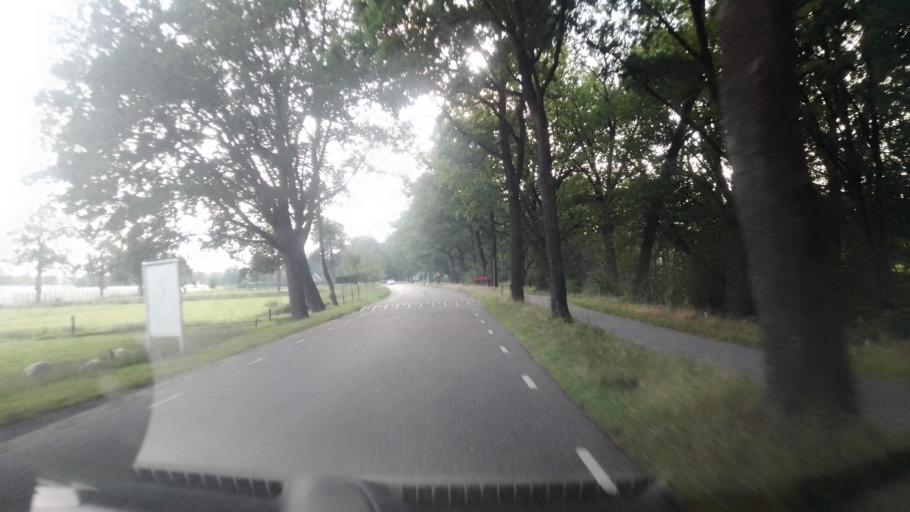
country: NL
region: Limburg
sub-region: Gemeente Peel en Maas
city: Maasbree
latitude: 51.3910
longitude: 5.9267
